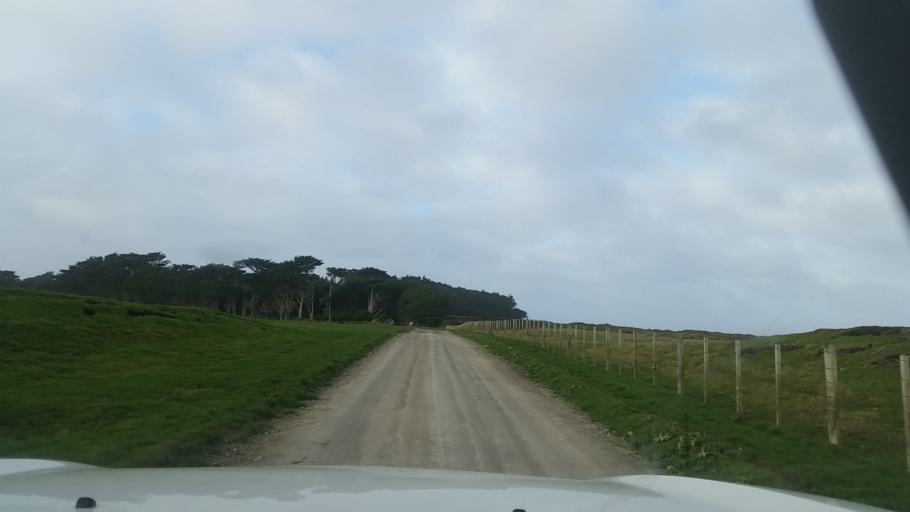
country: NZ
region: Chatham Islands
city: Waitangi
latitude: -43.7379
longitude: -176.2534
